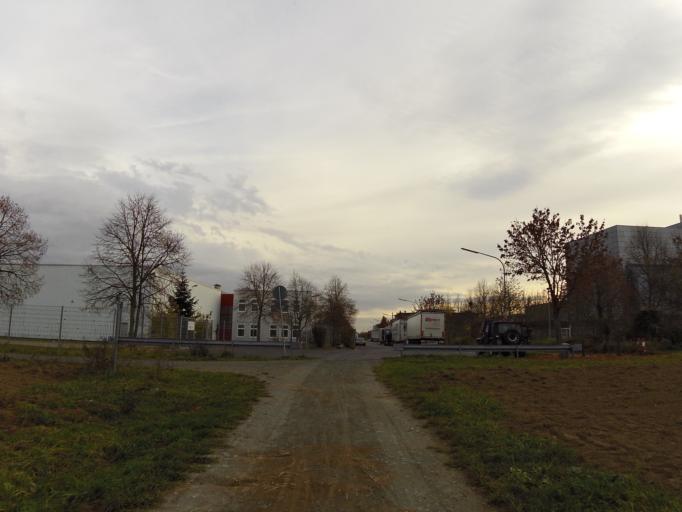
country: DE
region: Hesse
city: Morfelden-Walldorf
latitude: 49.9896
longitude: 8.5839
